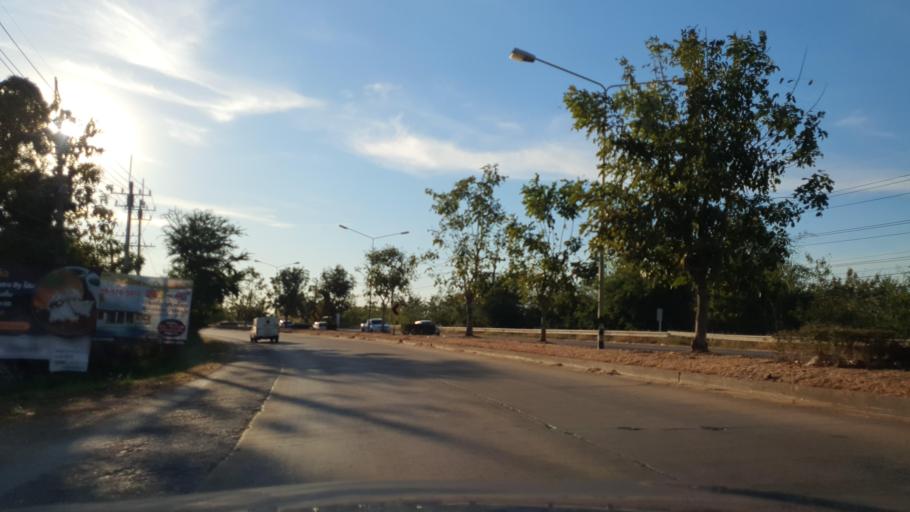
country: TH
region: Khon Kaen
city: Khon Kaen
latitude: 16.4373
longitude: 102.9003
